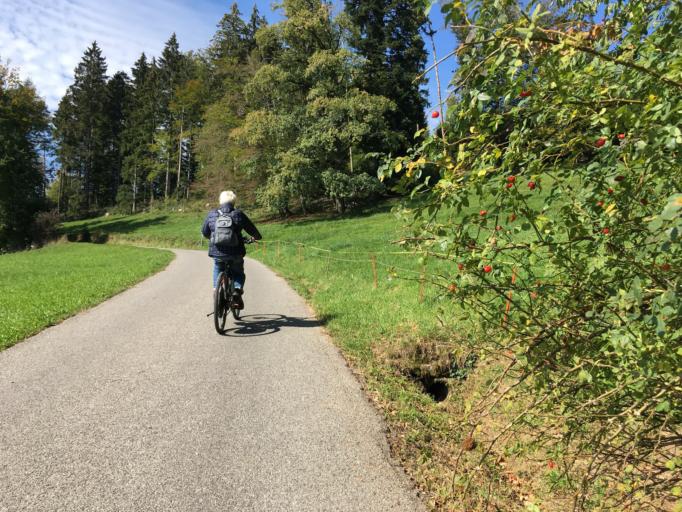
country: CH
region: Zurich
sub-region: Bezirk Hinwil
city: Baretswil
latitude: 47.3461
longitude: 8.8424
